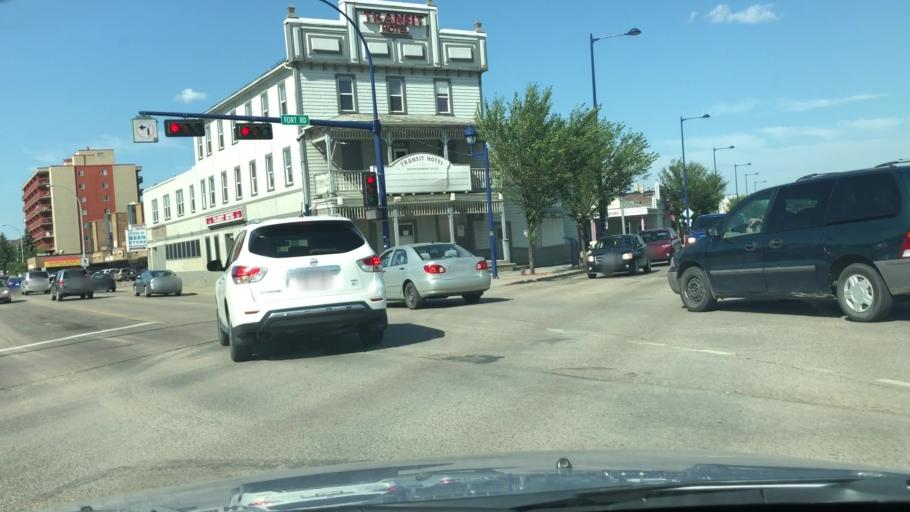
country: CA
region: Alberta
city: Edmonton
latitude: 53.5850
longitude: -113.4430
